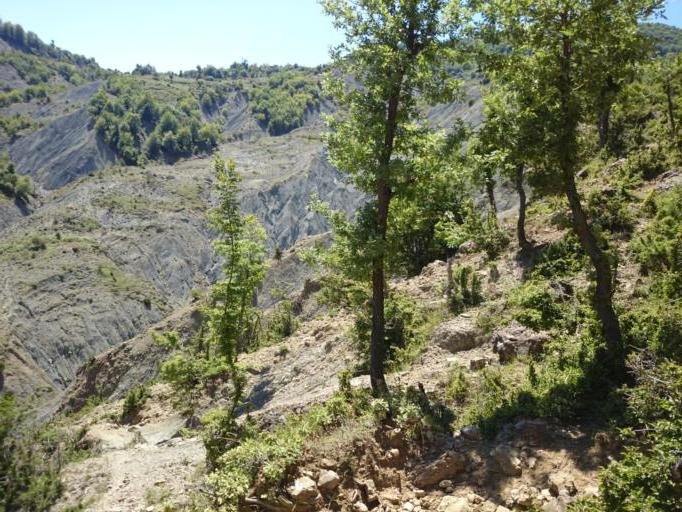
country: AL
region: Elbasan
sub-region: Rrethi i Gramshit
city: Porocan
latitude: 40.8943
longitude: 20.3035
